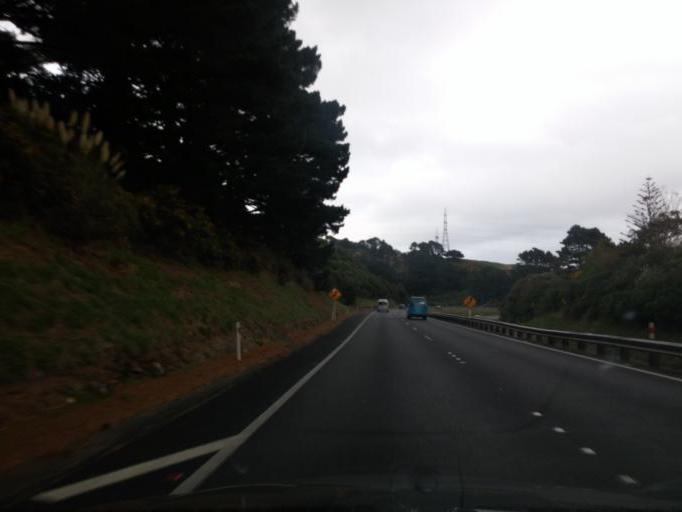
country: NZ
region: Wellington
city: Petone
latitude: -41.1913
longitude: 174.8309
